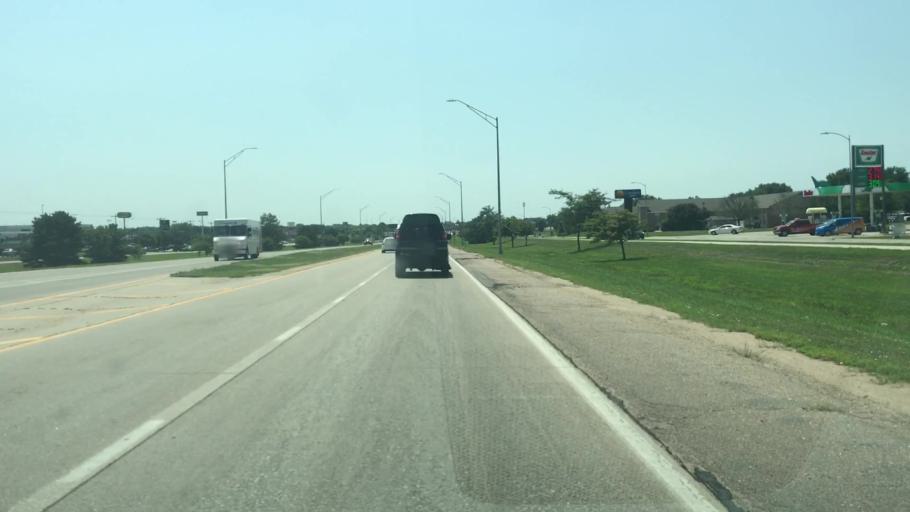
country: US
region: Nebraska
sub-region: Adams County
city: Hastings
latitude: 40.6178
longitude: -98.3832
